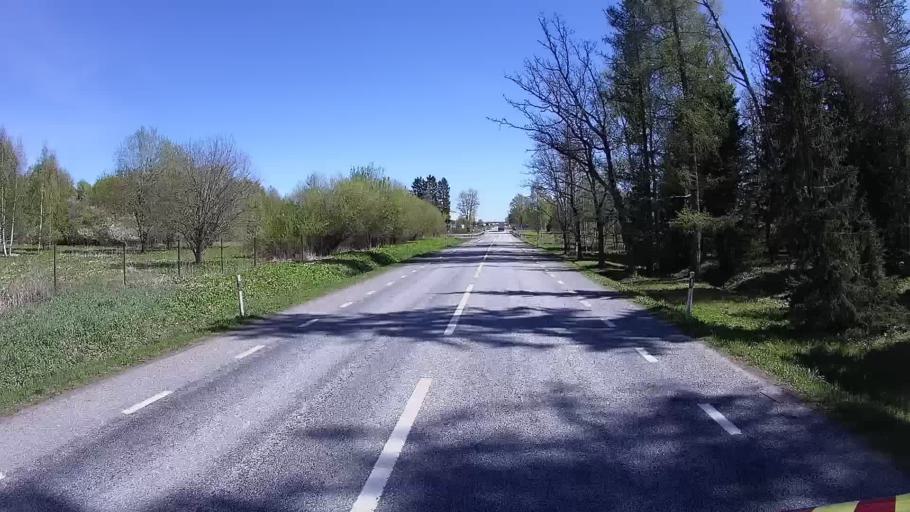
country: EE
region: Laeaene-Virumaa
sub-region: Tapa vald
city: Tapa
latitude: 59.2469
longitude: 25.6854
